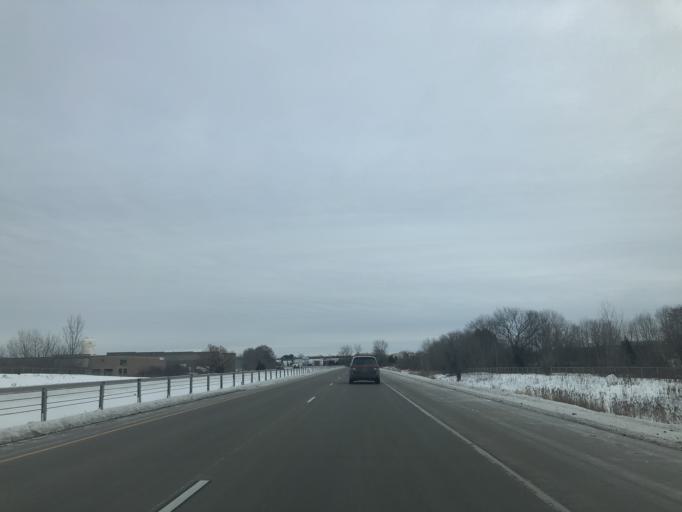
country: US
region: Minnesota
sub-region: Anoka County
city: Circle Pines
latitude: 45.1710
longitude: -93.1307
